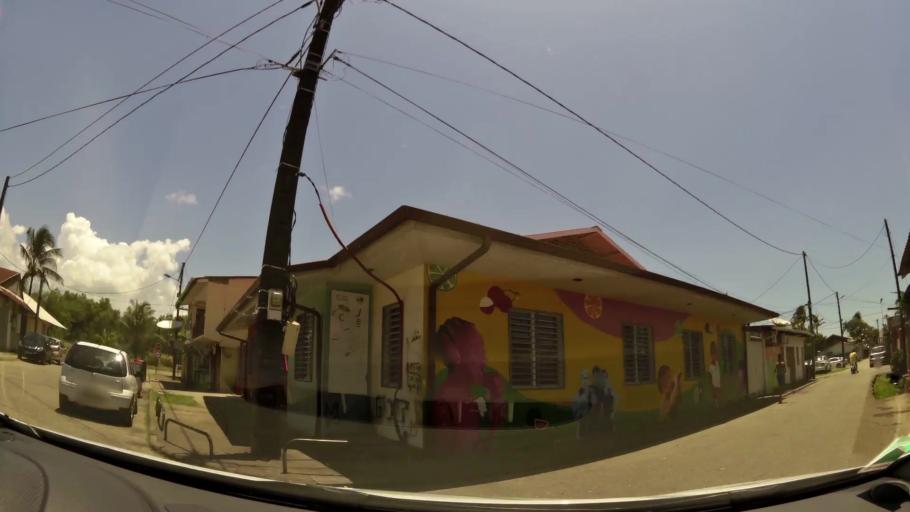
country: GF
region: Guyane
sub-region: Guyane
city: Cayenne
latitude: 4.9328
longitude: -52.3337
